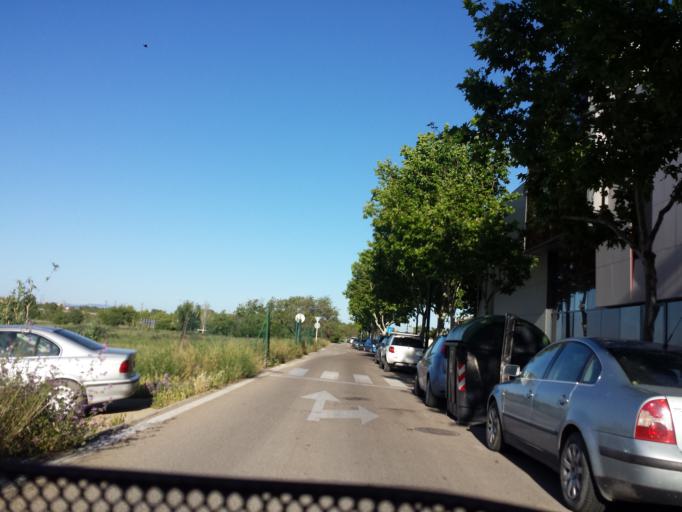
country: ES
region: Aragon
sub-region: Provincia de Zaragoza
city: Zaragoza
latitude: 41.6579
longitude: -0.8570
